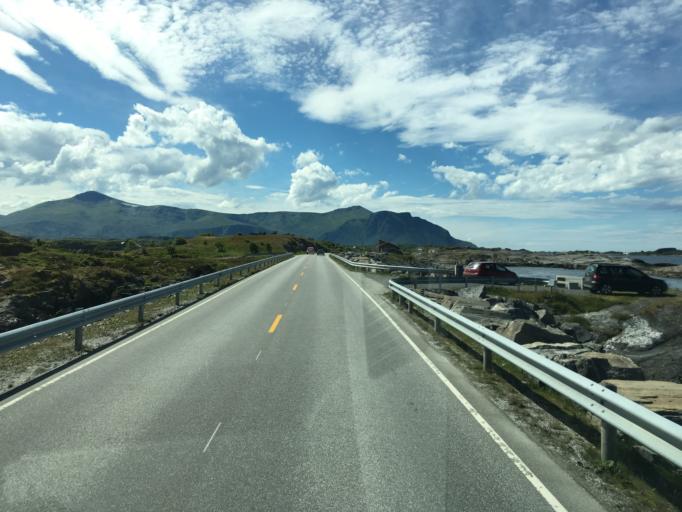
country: NO
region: More og Romsdal
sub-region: Eide
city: Eide
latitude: 63.0145
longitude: 7.3341
